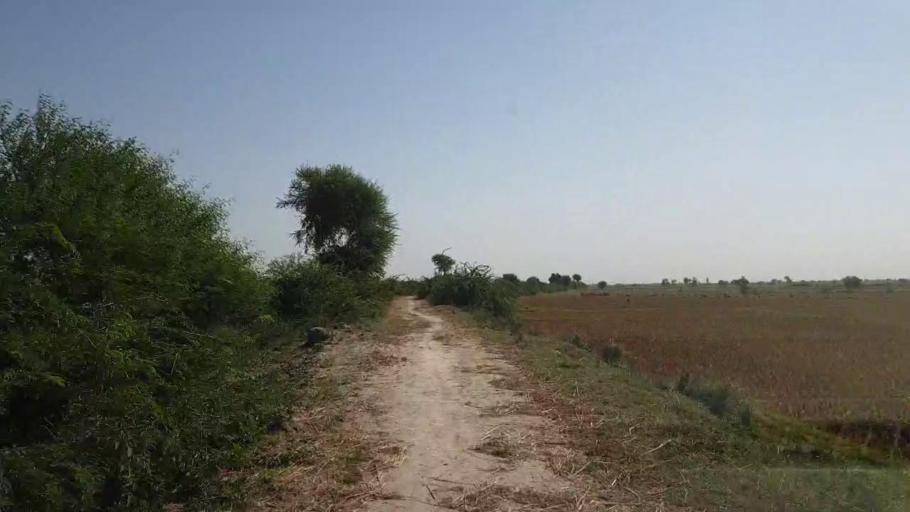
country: PK
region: Sindh
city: Kadhan
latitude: 24.6247
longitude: 68.9947
